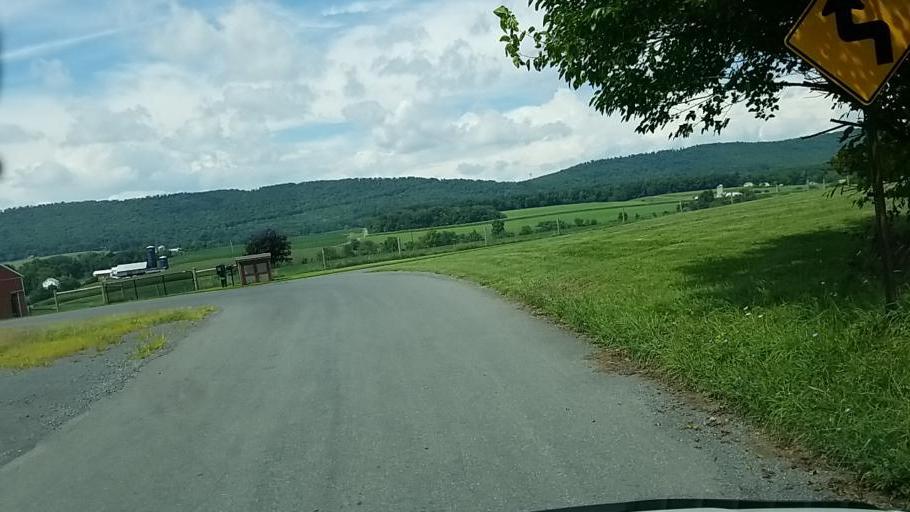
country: US
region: Pennsylvania
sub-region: Dauphin County
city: Elizabethville
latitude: 40.5816
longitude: -76.8767
